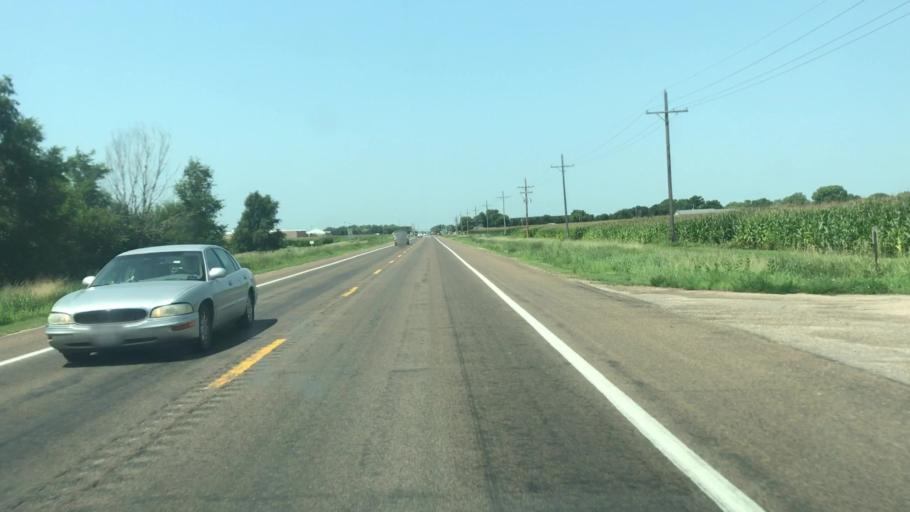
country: US
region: Nebraska
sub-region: Hall County
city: Grand Island
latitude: 40.8870
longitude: -98.3279
